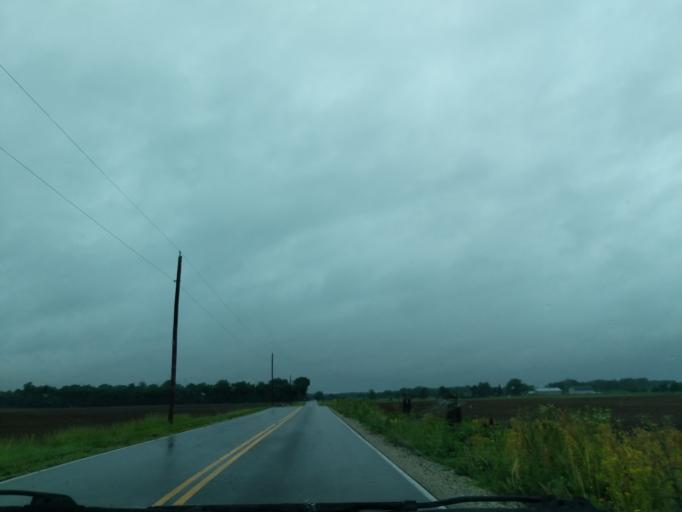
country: US
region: Indiana
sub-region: Madison County
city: Lapel
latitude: 40.0665
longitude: -85.9118
